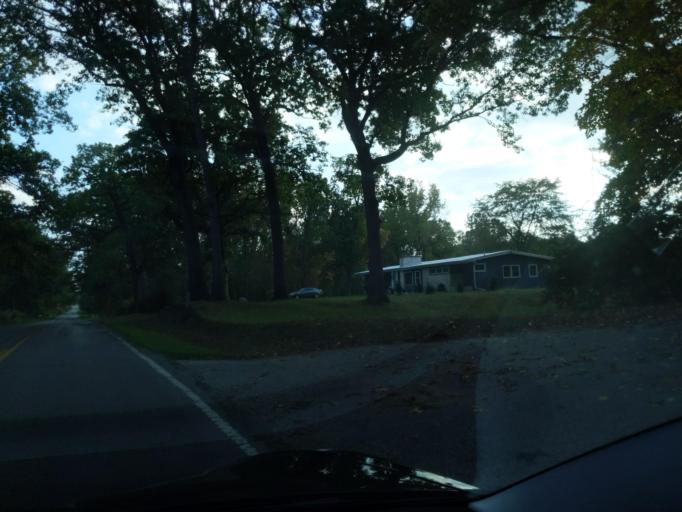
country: US
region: Michigan
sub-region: Jackson County
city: Jackson
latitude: 42.2888
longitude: -84.4831
